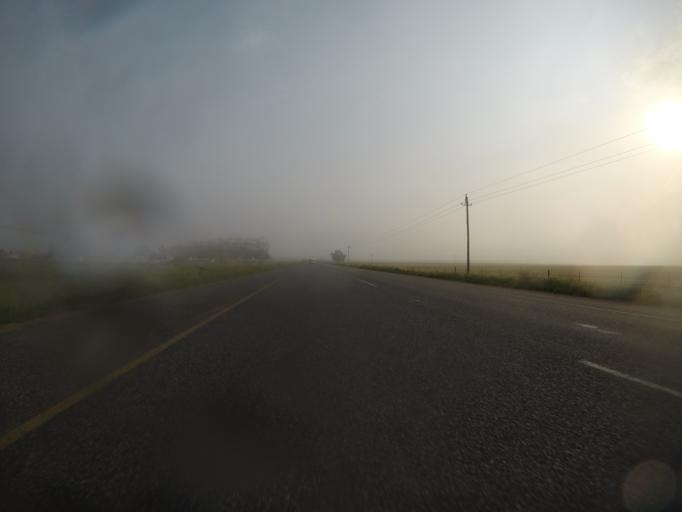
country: ZA
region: Western Cape
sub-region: City of Cape Town
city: Kraaifontein
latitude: -33.6684
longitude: 18.7074
